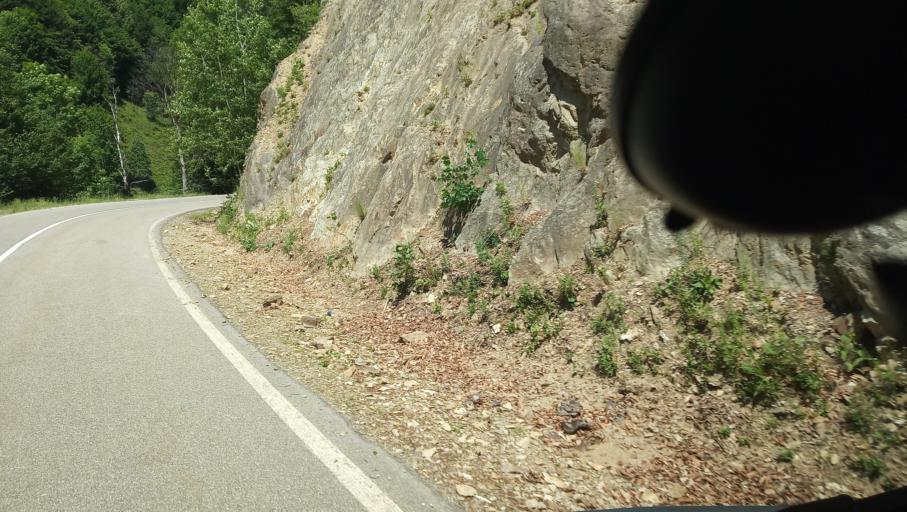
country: RO
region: Mehedinti
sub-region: Comuna Isverna
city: Isverna
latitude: 45.0429
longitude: 22.6199
